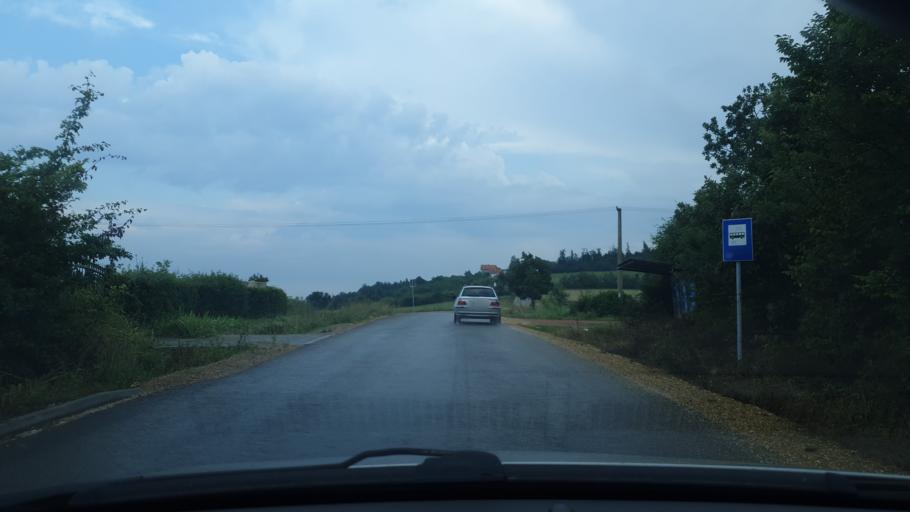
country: RS
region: Central Serbia
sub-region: Sumadijski Okrug
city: Kragujevac
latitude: 44.0636
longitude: 20.7846
